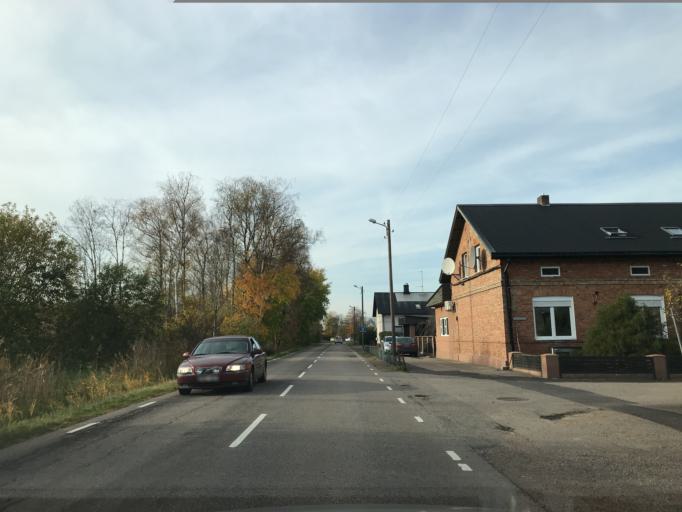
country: SE
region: Skane
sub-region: Helsingborg
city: Hyllinge
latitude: 56.1013
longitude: 12.8702
